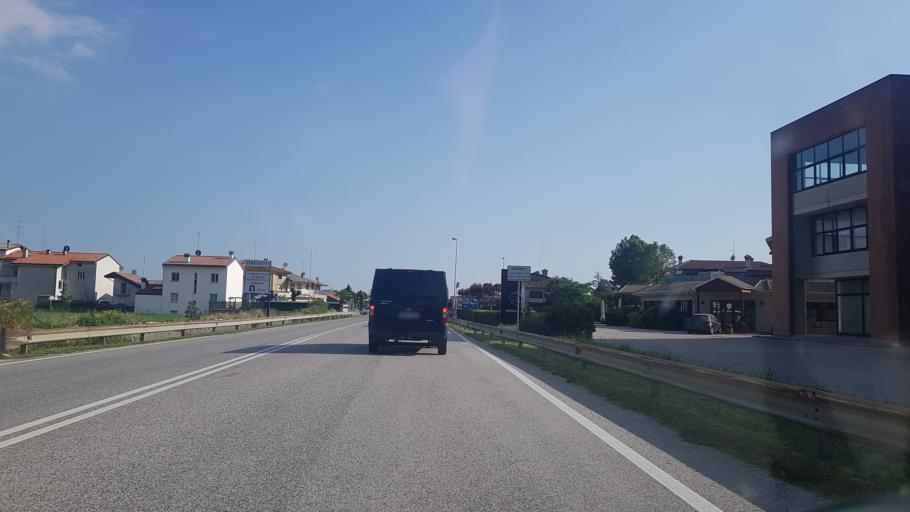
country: IT
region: Friuli Venezia Giulia
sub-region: Provincia di Udine
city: Gemona
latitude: 46.2823
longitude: 13.1097
